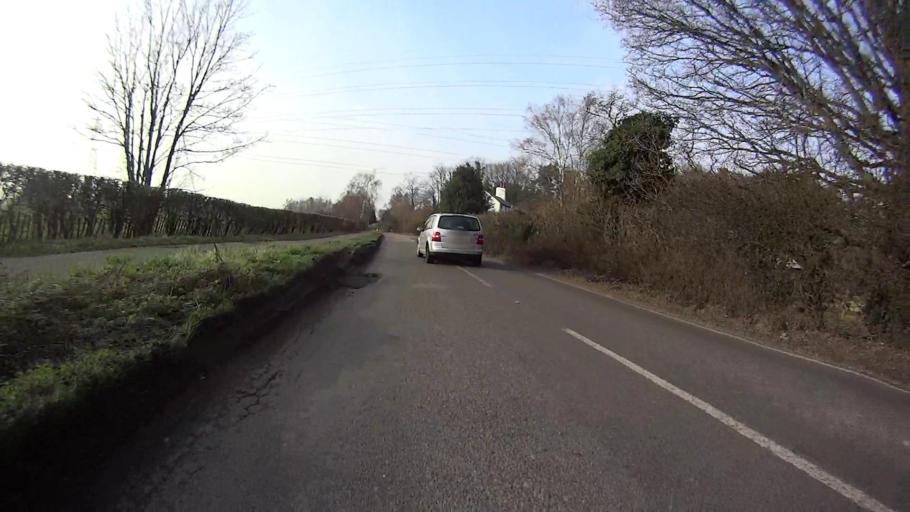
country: GB
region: England
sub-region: West Sussex
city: Copthorne
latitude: 51.1137
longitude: -0.1232
